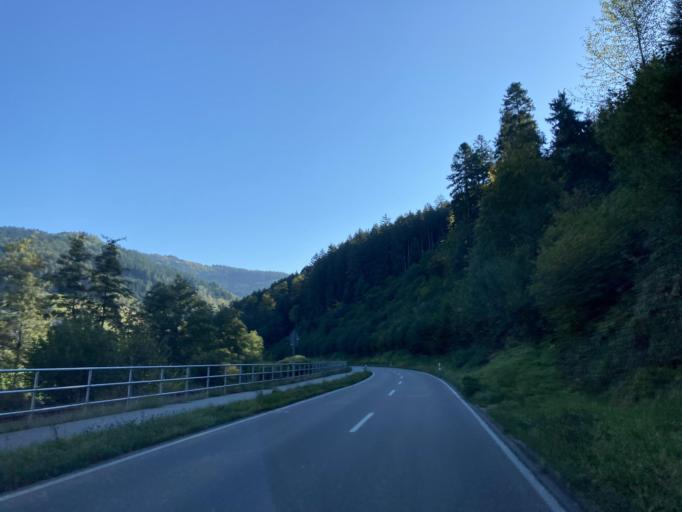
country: DE
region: Baden-Wuerttemberg
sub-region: Freiburg Region
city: Wolfach
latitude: 48.2787
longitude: 8.2081
